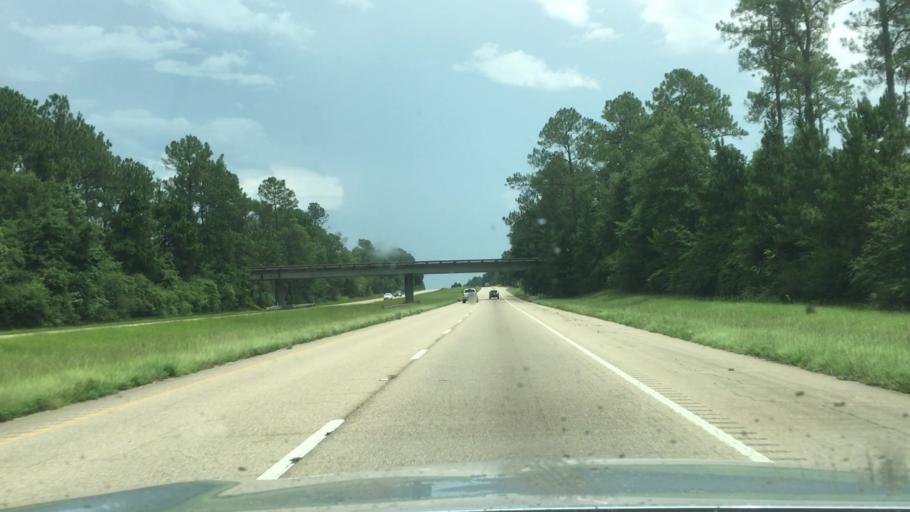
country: US
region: Mississippi
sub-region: Lamar County
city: Lumberton
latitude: 30.9229
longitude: -89.4587
